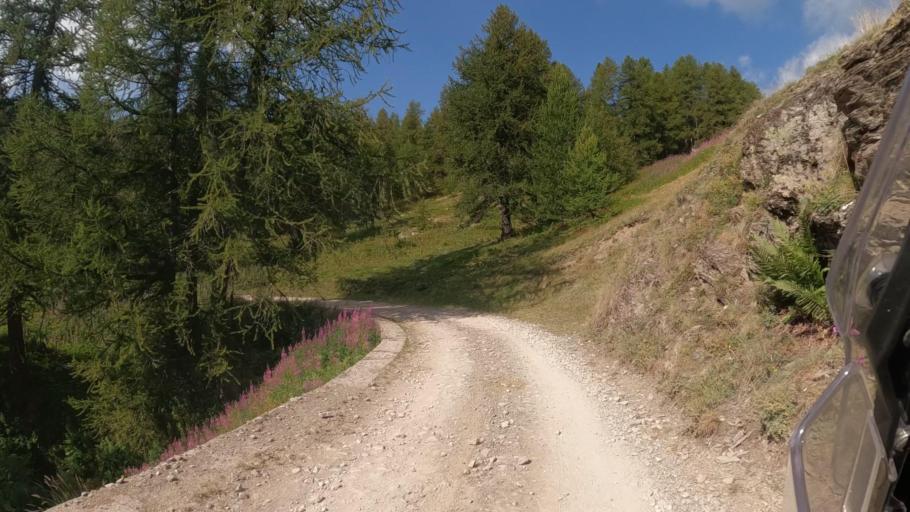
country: IT
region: Piedmont
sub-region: Provincia di Cuneo
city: Briga Alta
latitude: 44.1160
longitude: 7.6984
